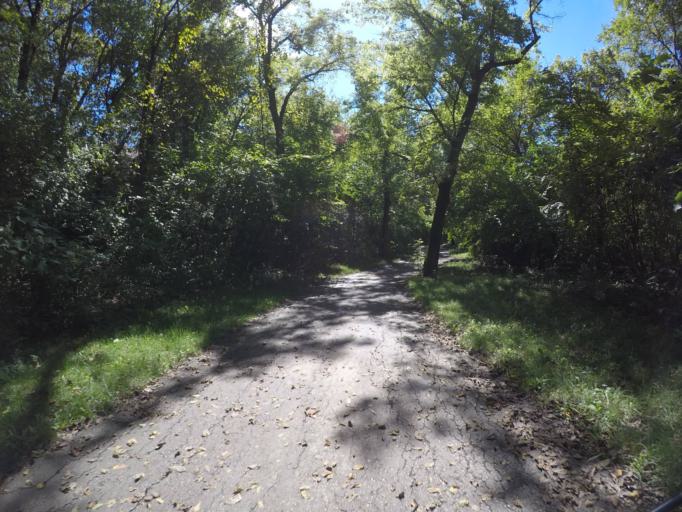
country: US
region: Kansas
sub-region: Johnson County
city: Lenexa
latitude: 38.9044
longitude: -94.7322
